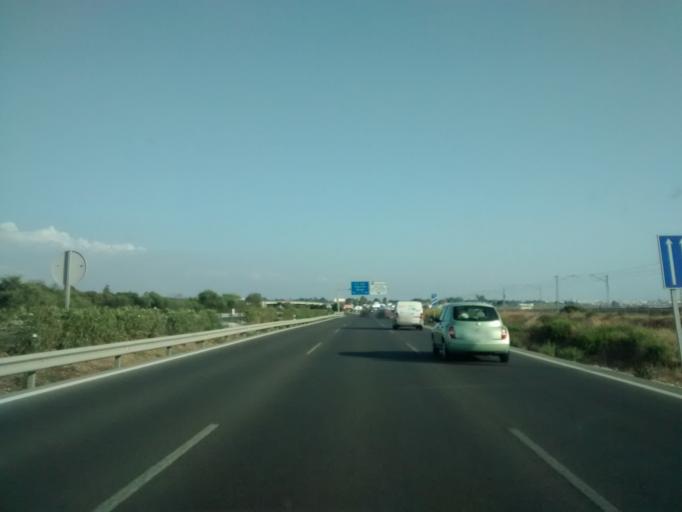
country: ES
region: Andalusia
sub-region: Provincia de Cadiz
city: Chiclana de la Frontera
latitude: 36.4479
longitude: -6.1487
